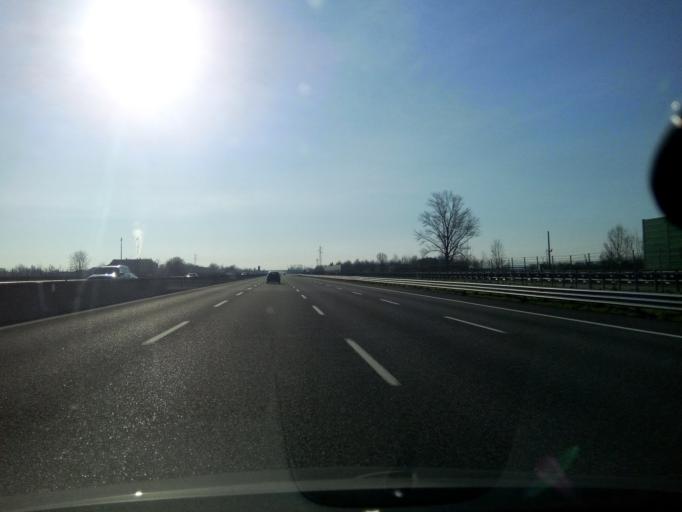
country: IT
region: Emilia-Romagna
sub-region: Provincia di Modena
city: Montale
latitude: 44.6048
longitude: 10.9166
